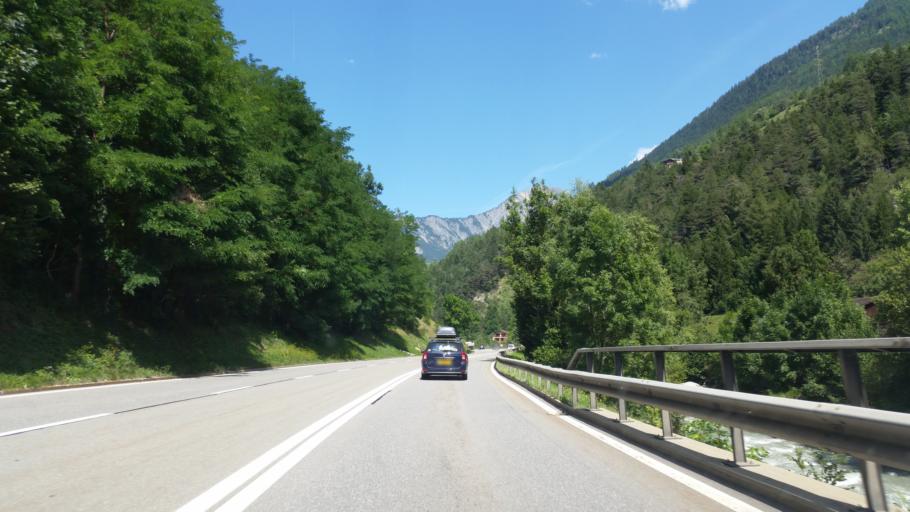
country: CH
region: Valais
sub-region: Entremont District
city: Orsieres
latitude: 46.0491
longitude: 7.1481
